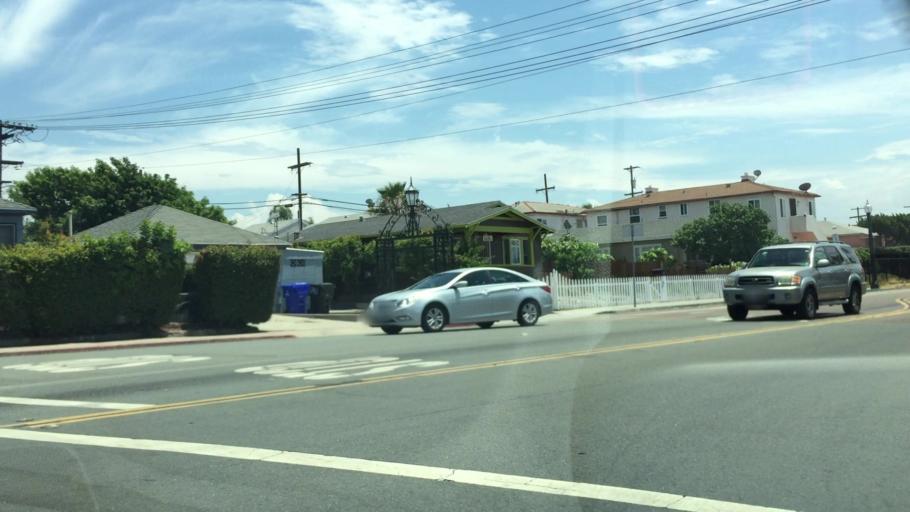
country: US
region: California
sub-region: San Diego County
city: Lemon Grove
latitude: 32.7590
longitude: -117.0922
